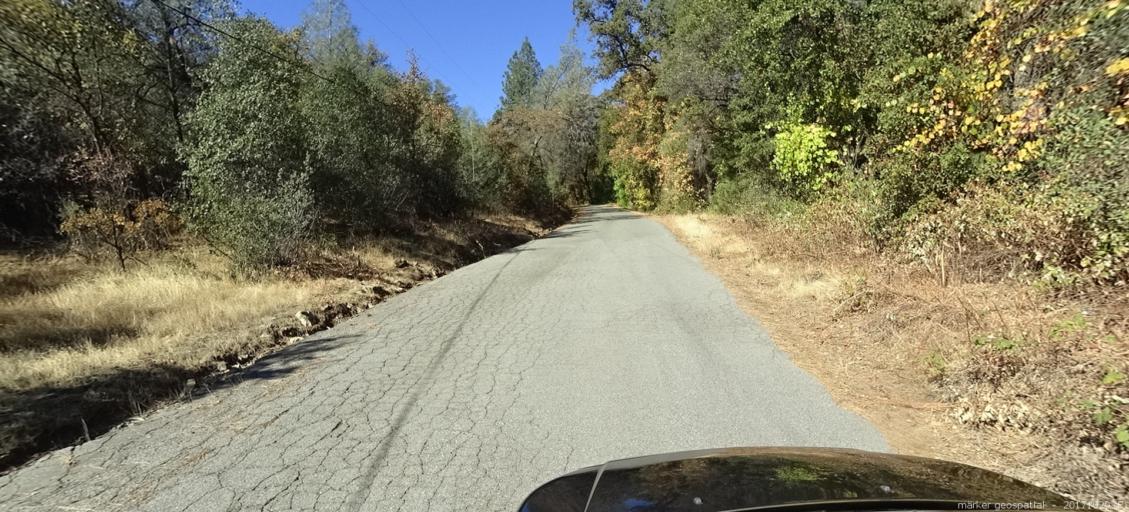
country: US
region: California
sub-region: Shasta County
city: Shasta
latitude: 40.4883
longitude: -122.6806
